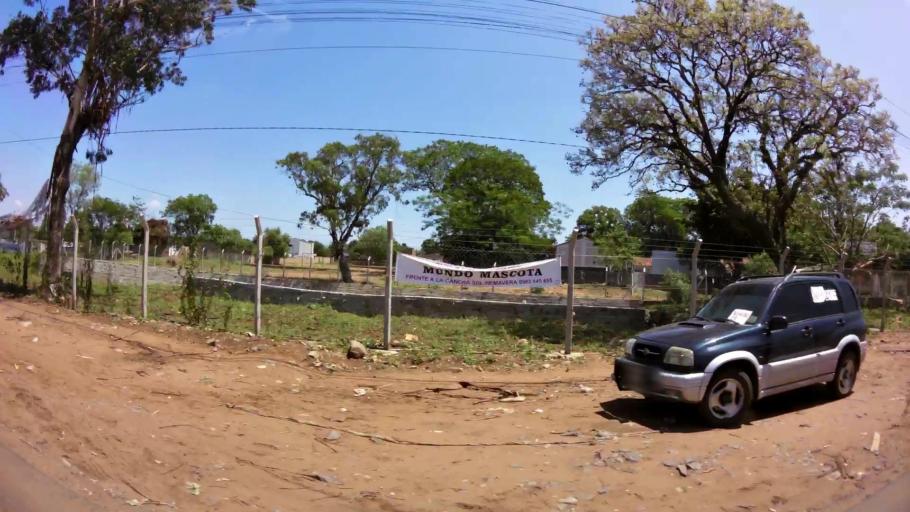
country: PY
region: Central
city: Nemby
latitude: -25.3928
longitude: -57.5274
